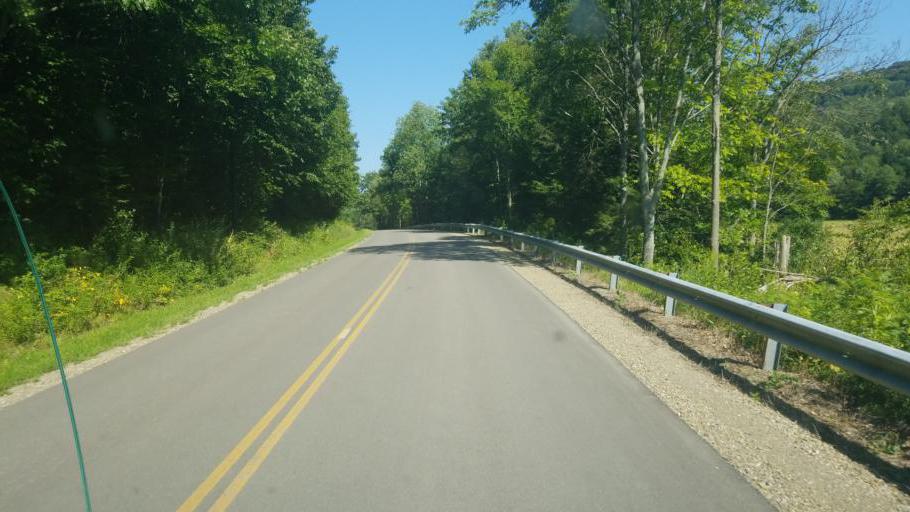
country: US
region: New York
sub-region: Allegany County
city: Wellsville
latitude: 42.0220
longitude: -77.9712
